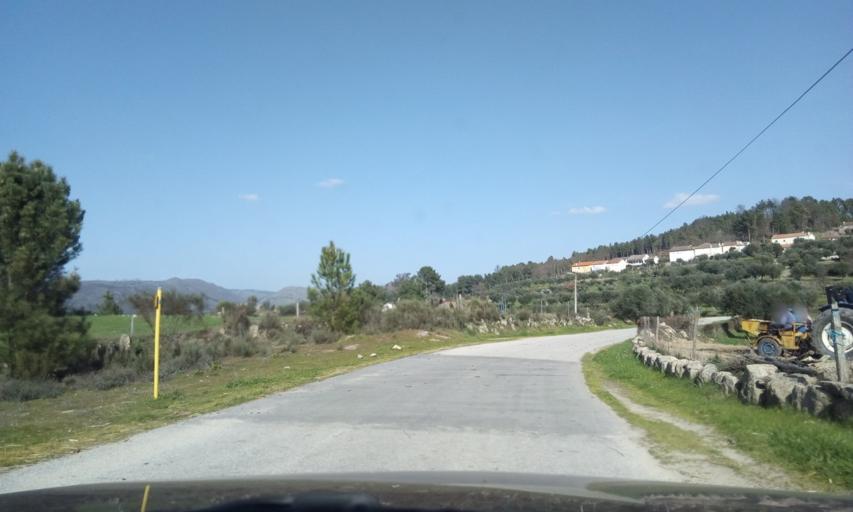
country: PT
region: Guarda
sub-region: Celorico da Beira
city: Celorico da Beira
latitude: 40.6536
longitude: -7.4141
